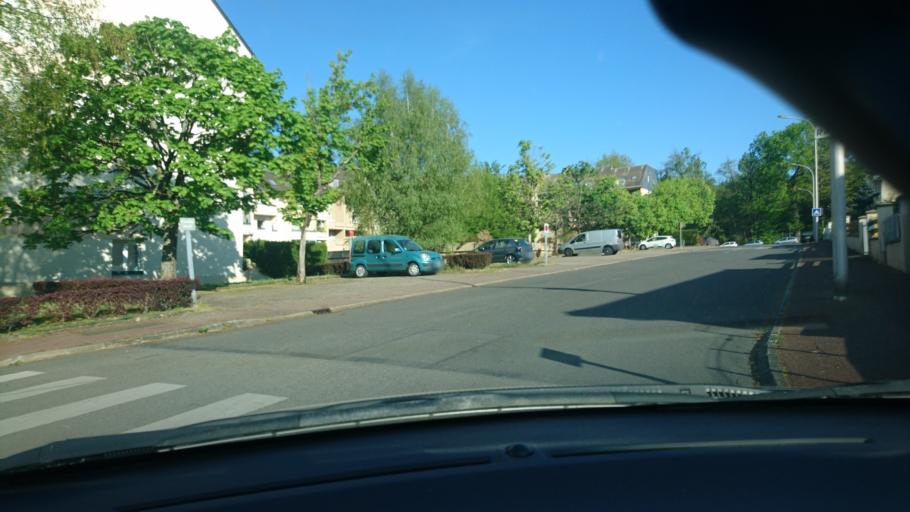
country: FR
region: Limousin
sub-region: Departement de la Haute-Vienne
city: Limoges
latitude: 45.8567
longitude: 1.2757
